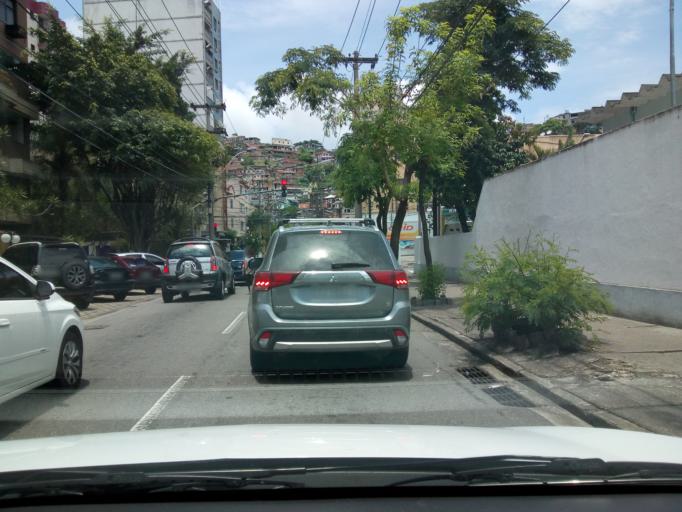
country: BR
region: Rio de Janeiro
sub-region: Niteroi
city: Niteroi
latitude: -22.9088
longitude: -43.1030
